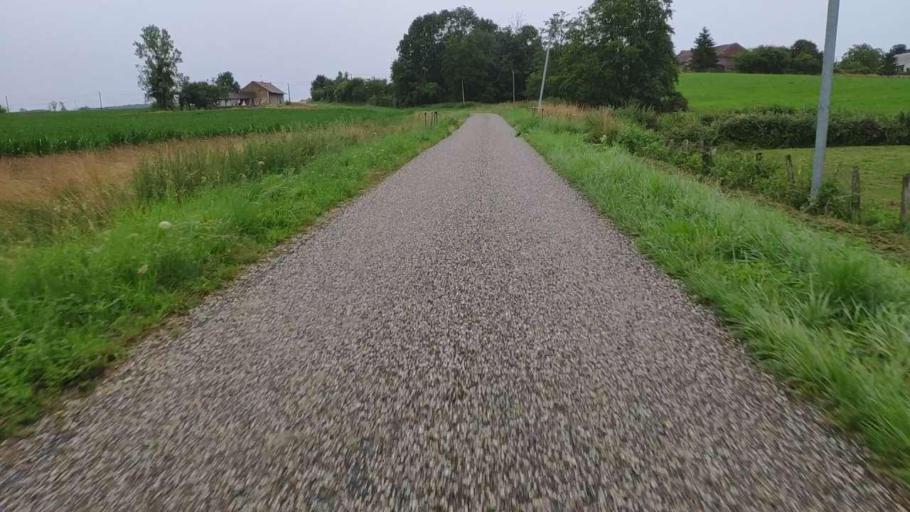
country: FR
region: Franche-Comte
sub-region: Departement du Jura
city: Chaussin
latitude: 46.8734
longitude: 5.4163
